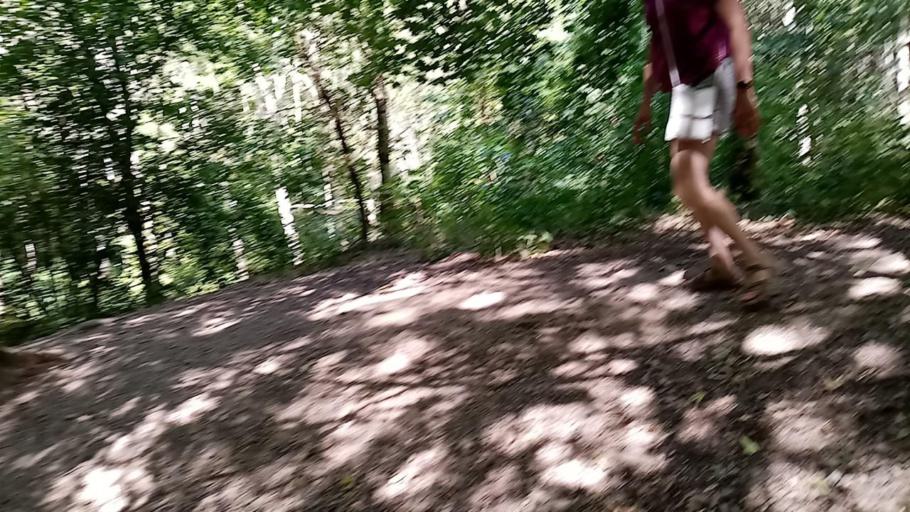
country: FR
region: Rhone-Alpes
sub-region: Departement du Rhone
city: Grandris
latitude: 46.0086
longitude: 4.5423
